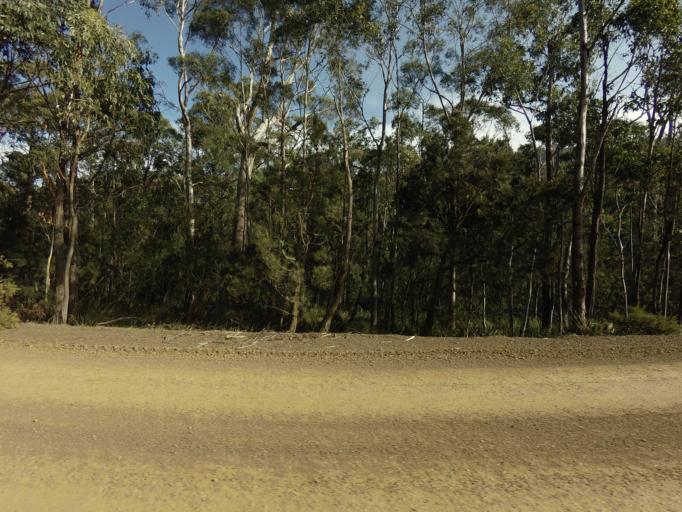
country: AU
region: Tasmania
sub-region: Huon Valley
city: Huonville
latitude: -43.0600
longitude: 147.0948
